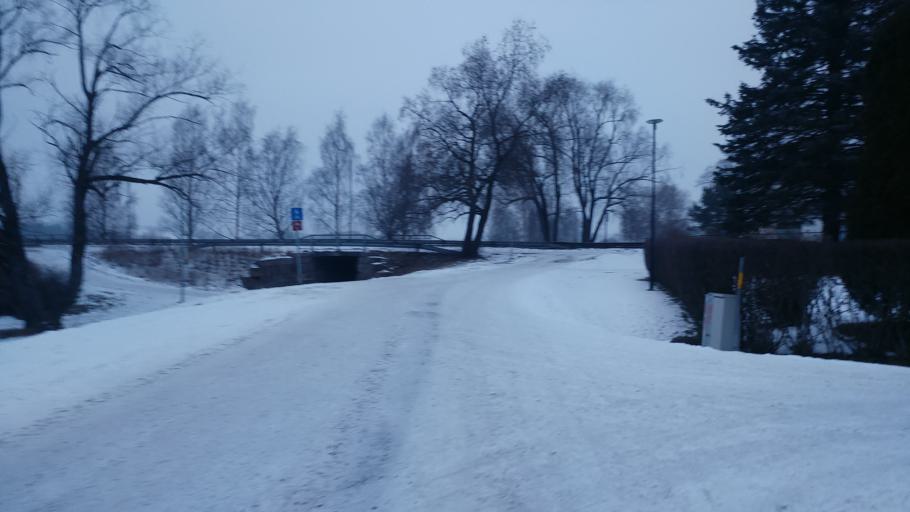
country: NO
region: Akershus
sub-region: Skedsmo
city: Lillestrom
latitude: 59.9567
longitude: 11.0309
